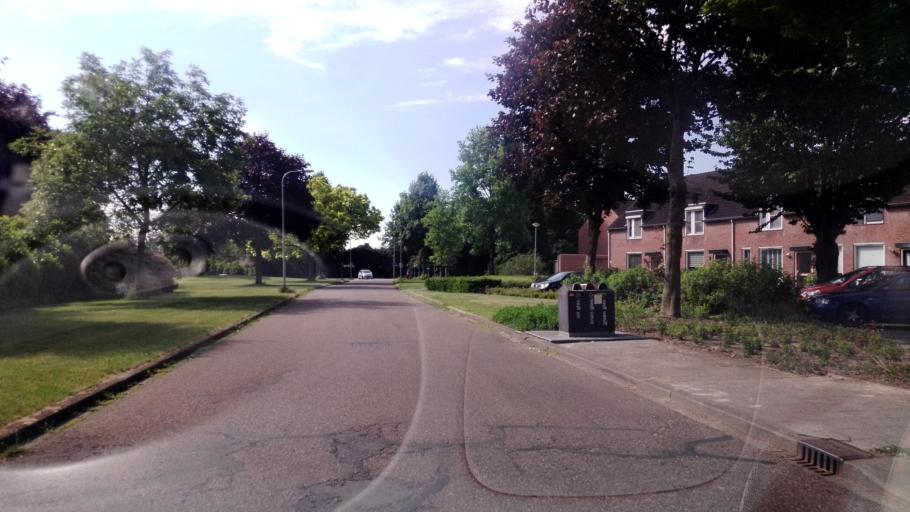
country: NL
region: Limburg
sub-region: Gemeente Peel en Maas
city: Maasbree
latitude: 51.3223
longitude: 5.9917
